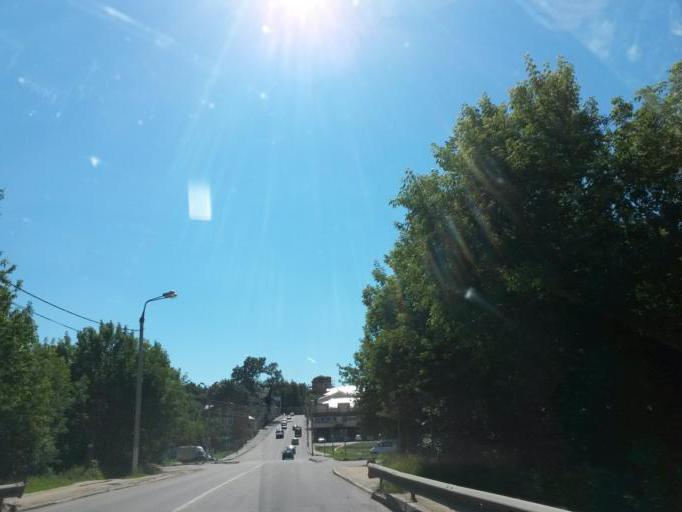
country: RU
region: Moskovskaya
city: Serpukhov
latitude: 54.9149
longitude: 37.3986
